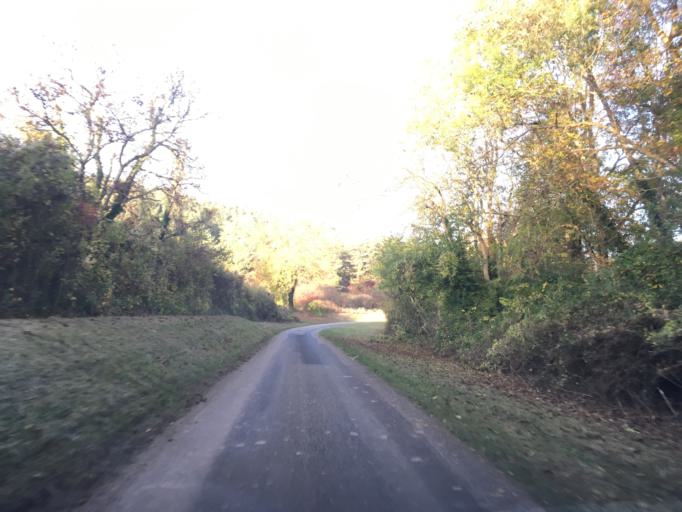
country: FR
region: Haute-Normandie
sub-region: Departement de l'Eure
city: Heudreville-sur-Eure
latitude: 49.1001
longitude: 1.2248
